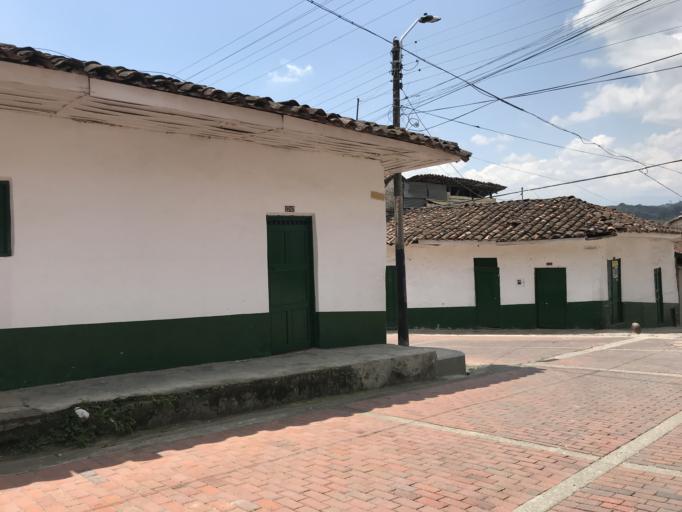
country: CO
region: Huila
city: San Agustin
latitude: 1.8844
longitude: -76.2716
